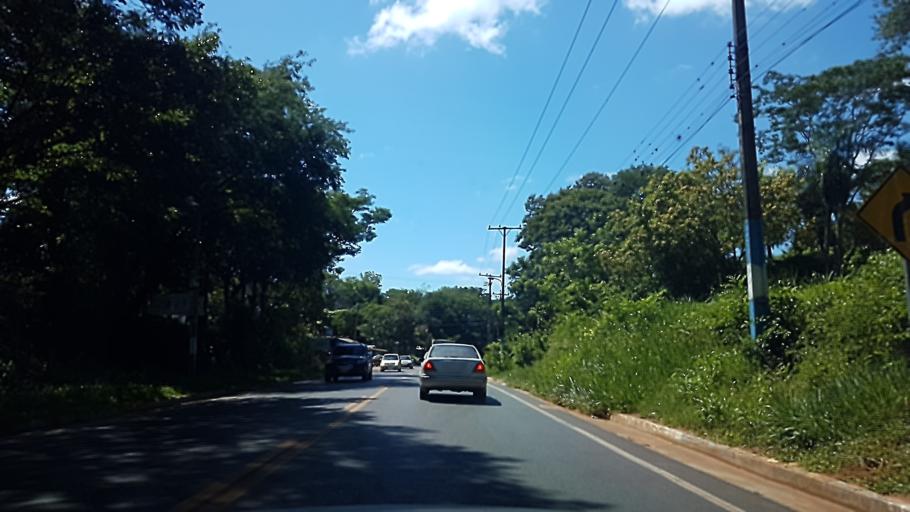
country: PY
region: Central
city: San Lorenzo
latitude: -25.2950
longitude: -57.4759
